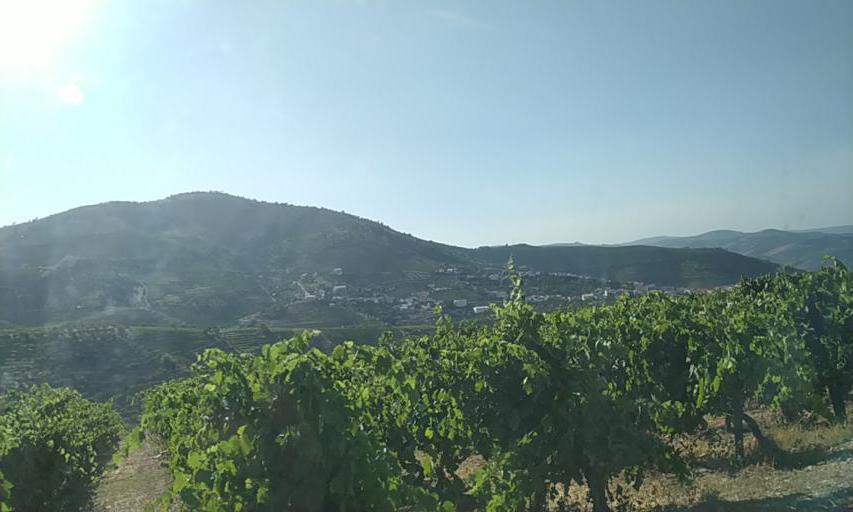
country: PT
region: Viseu
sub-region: Sao Joao da Pesqueira
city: Sao Joao da Pesqueira
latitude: 41.1758
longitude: -7.4064
